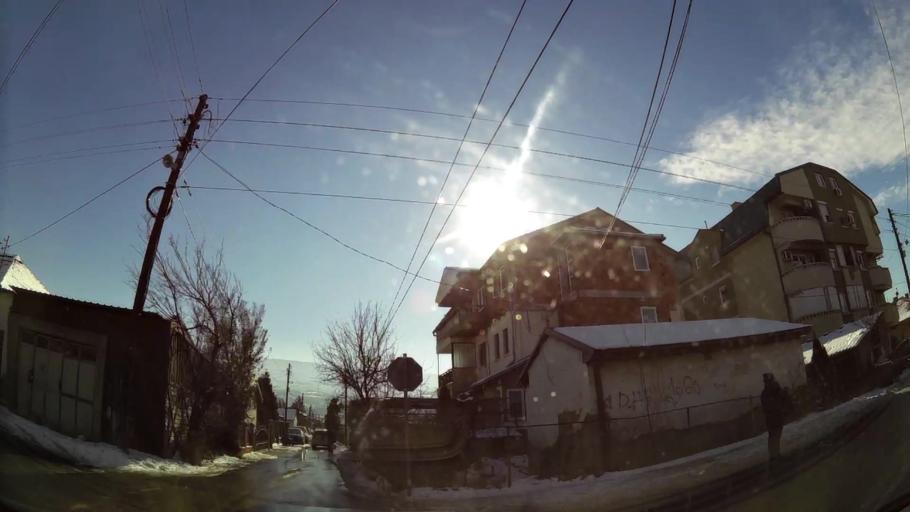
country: MK
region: Saraj
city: Saraj
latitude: 42.0076
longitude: 21.3544
